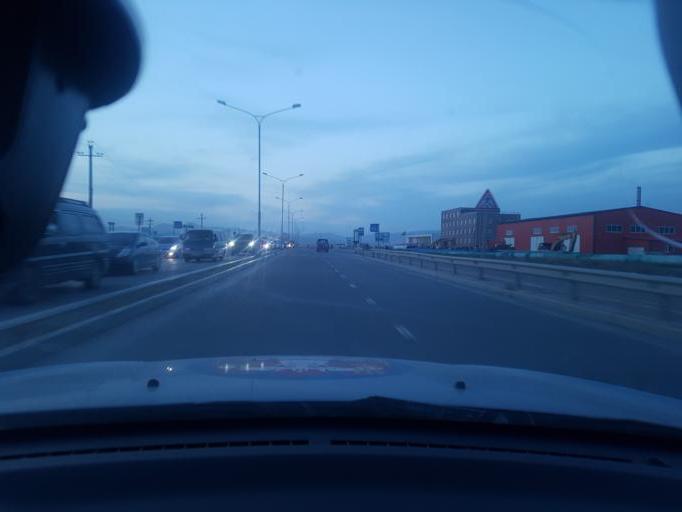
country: MN
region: Ulaanbaatar
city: Ulaanbaatar
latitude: 47.8796
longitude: 106.7847
